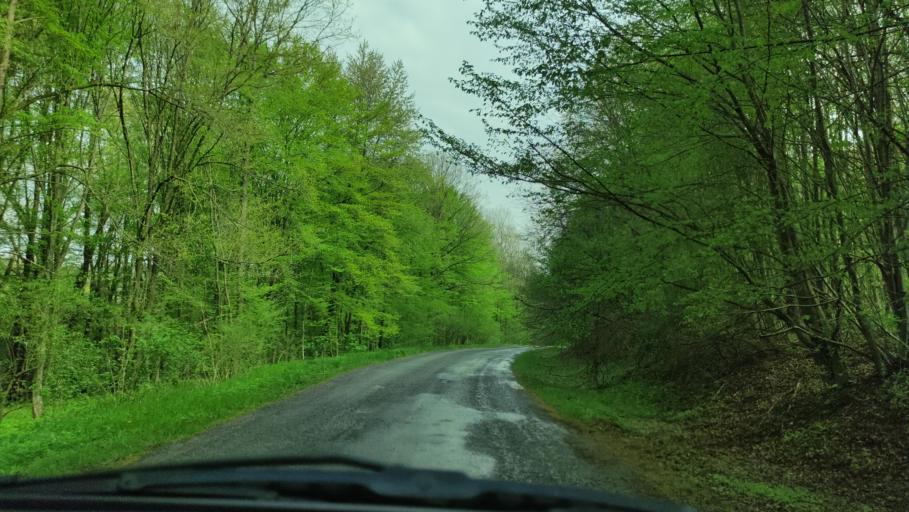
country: HU
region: Baranya
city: Komlo
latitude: 46.2614
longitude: 18.2125
